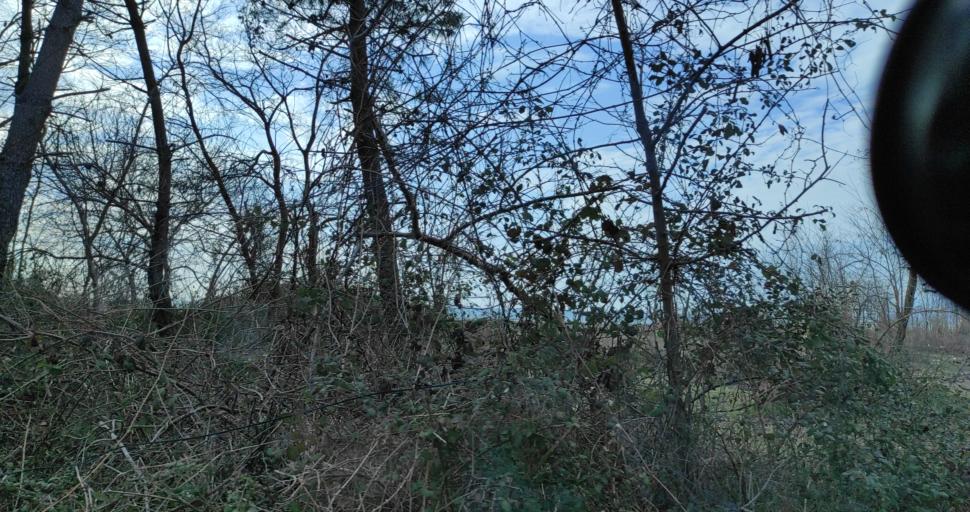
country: AL
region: Lezhe
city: Shengjin
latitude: 41.7798
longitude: 19.6034
